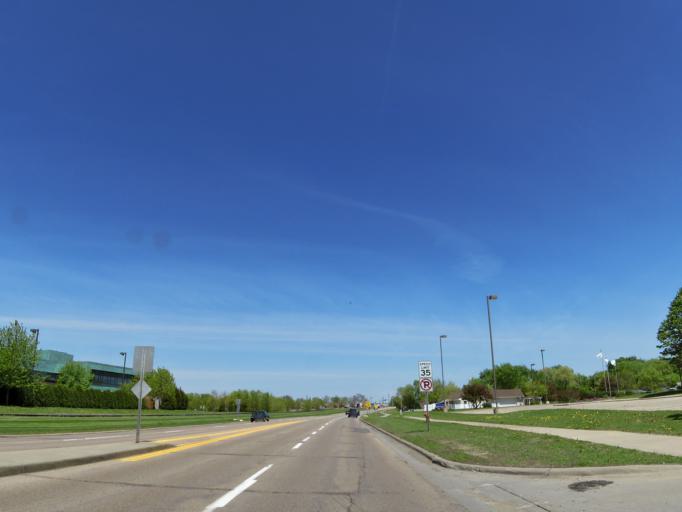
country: US
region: Minnesota
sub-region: Hennepin County
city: Bloomington
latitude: 44.8234
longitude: -93.3024
